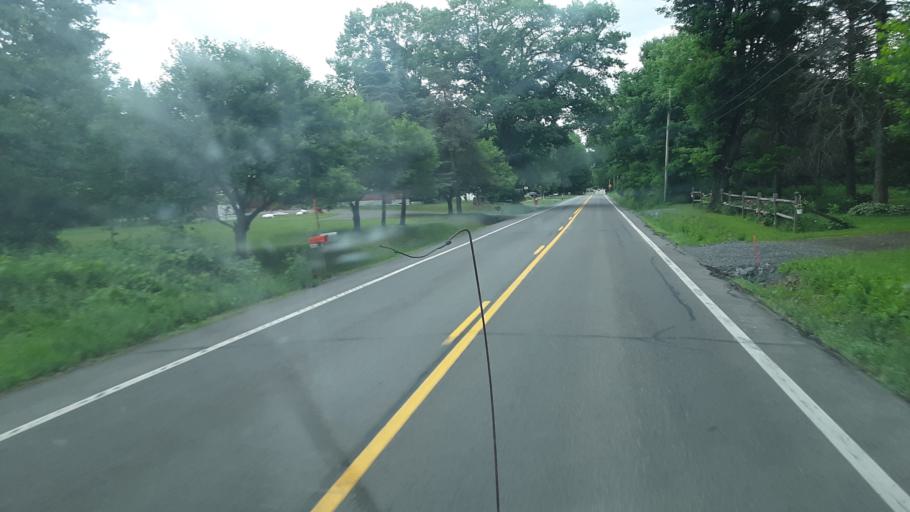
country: US
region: New York
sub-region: Oneida County
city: Rome
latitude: 43.3195
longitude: -75.4761
